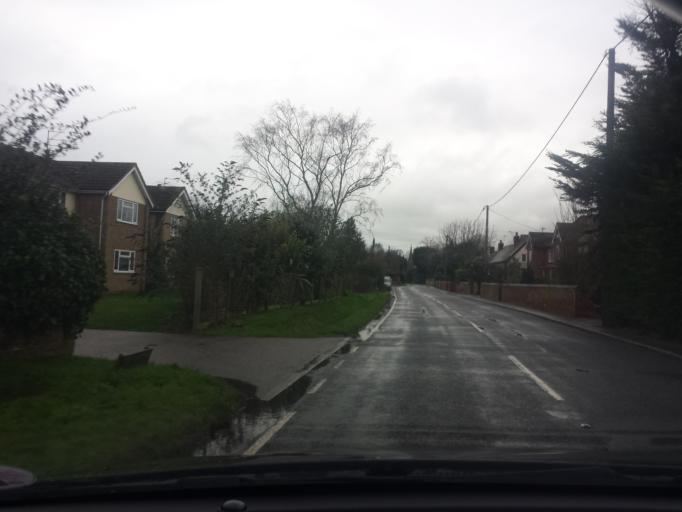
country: GB
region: England
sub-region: Essex
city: Little Clacton
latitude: 51.8749
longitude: 1.1194
